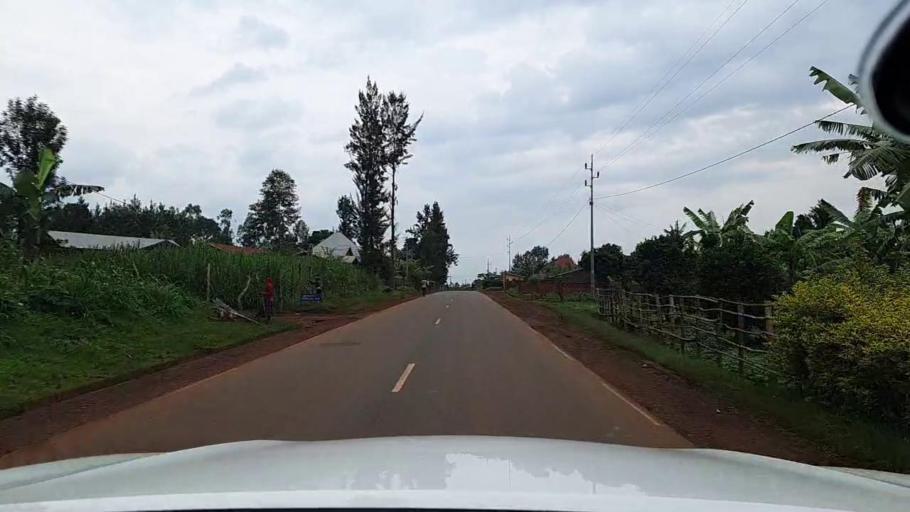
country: RW
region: Western Province
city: Cyangugu
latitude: -2.6190
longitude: 28.9453
